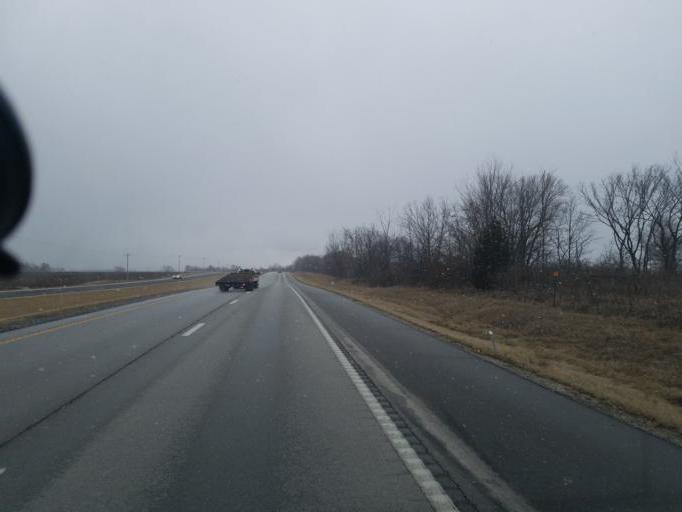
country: US
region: Missouri
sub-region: Macon County
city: Macon
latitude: 39.8738
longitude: -92.4774
